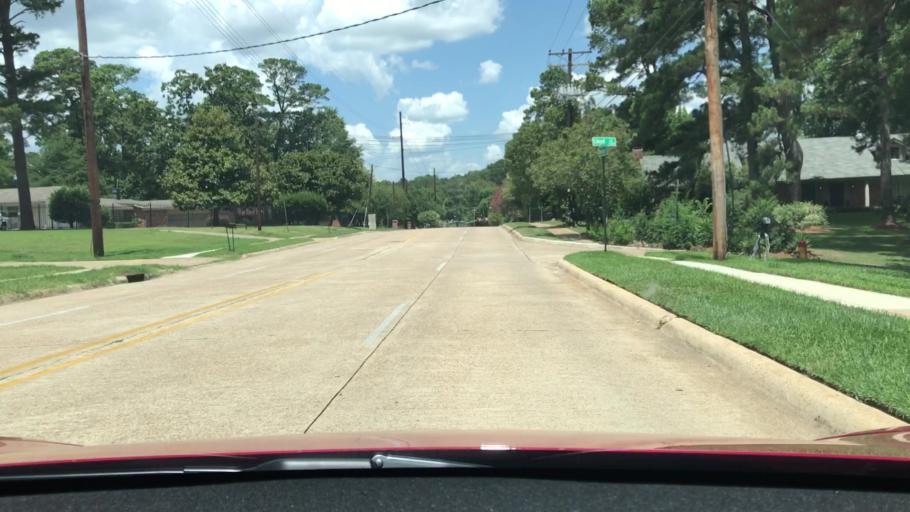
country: US
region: Louisiana
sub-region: Bossier Parish
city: Bossier City
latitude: 32.4408
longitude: -93.7369
